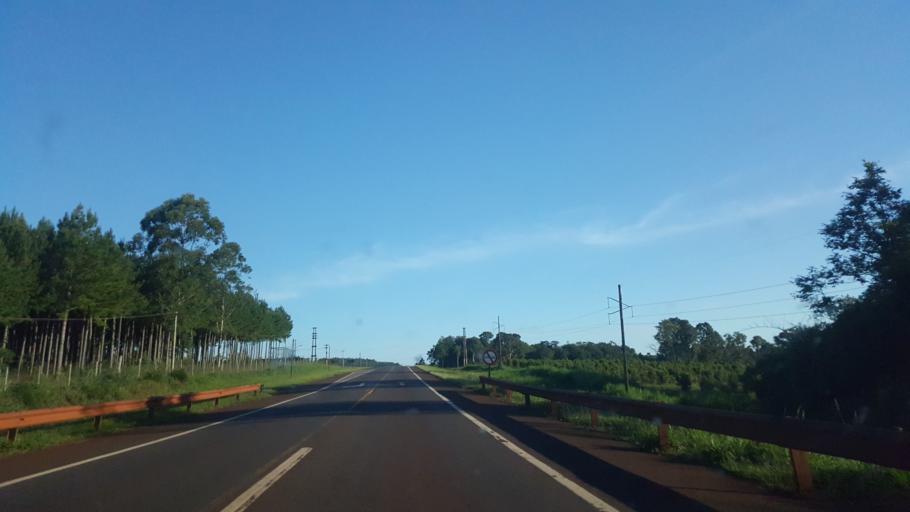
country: AR
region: Misiones
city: Caraguatay
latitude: -26.6485
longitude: -54.7542
